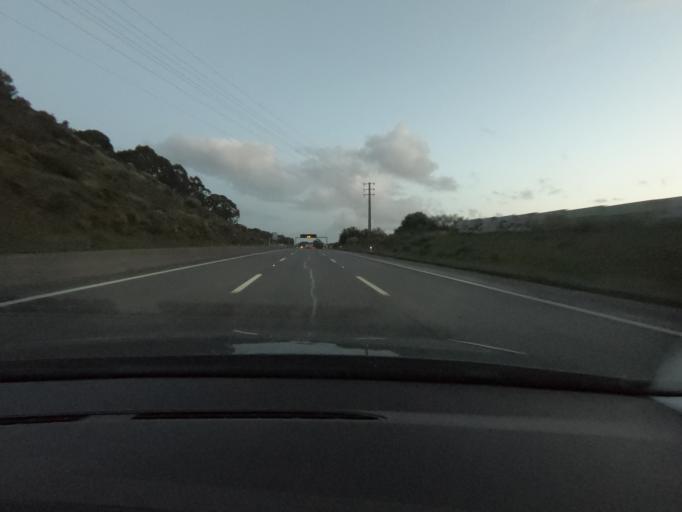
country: PT
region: Lisbon
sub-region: Oeiras
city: Barcarena
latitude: 38.7308
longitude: -9.2745
